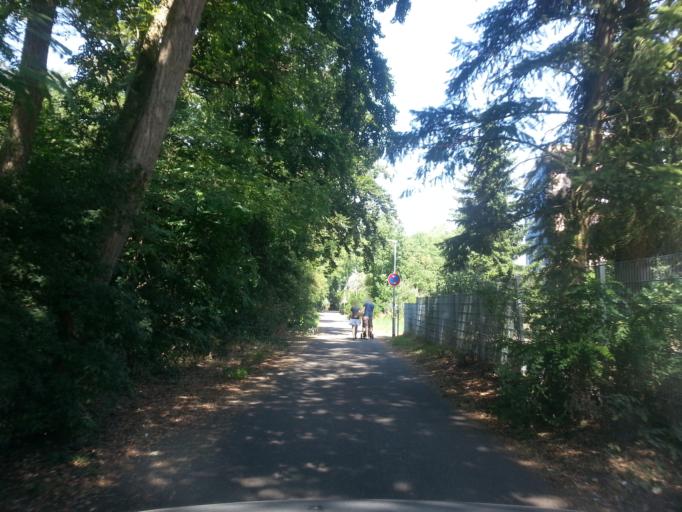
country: DE
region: Hesse
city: Lorsch
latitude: 49.6501
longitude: 8.5558
